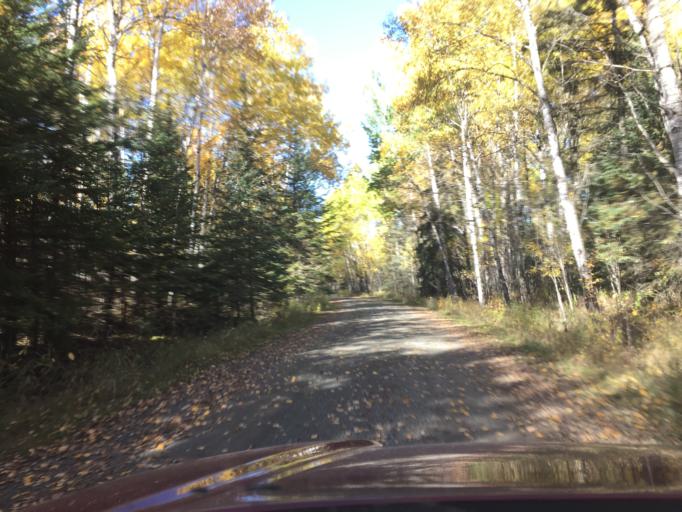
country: US
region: Minnesota
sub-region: Lake of the Woods County
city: Baudette
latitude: 48.2851
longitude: -94.5629
